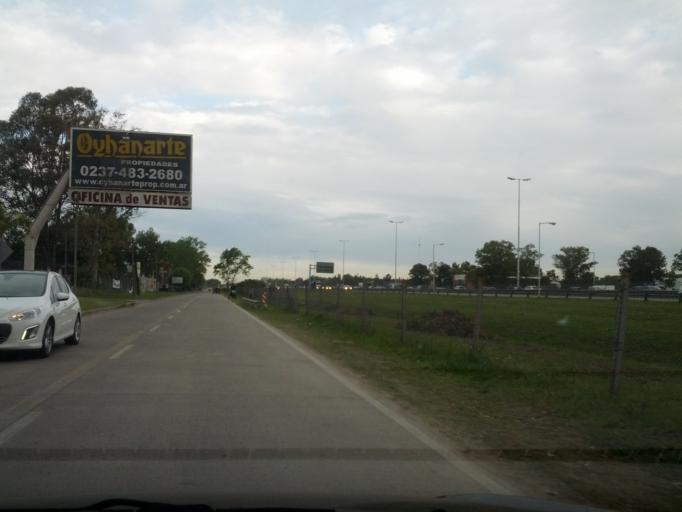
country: AR
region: Buenos Aires
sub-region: Partido de General Rodriguez
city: General Rodriguez
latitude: -34.6104
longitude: -58.8675
